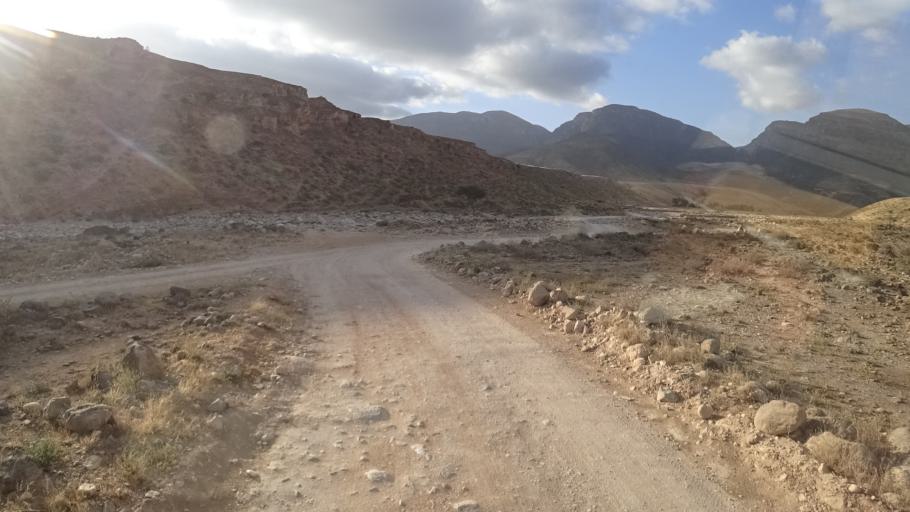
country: OM
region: Zufar
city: Salalah
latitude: 16.9820
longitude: 53.8512
